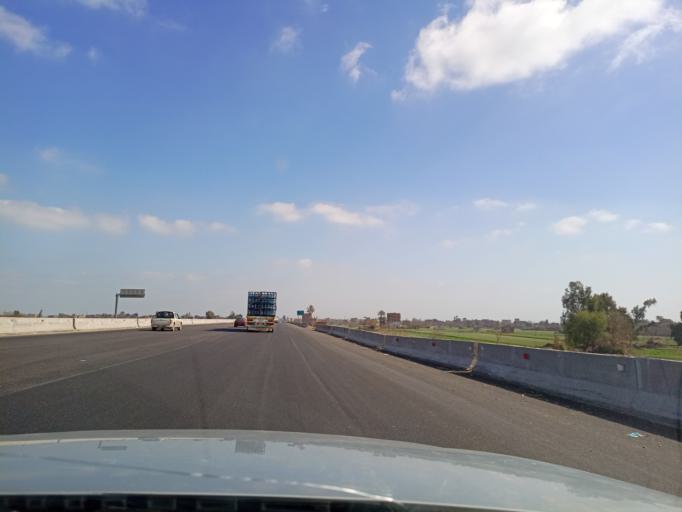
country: EG
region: Muhafazat al Minufiyah
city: Al Bajur
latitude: 30.4082
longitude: 31.0495
